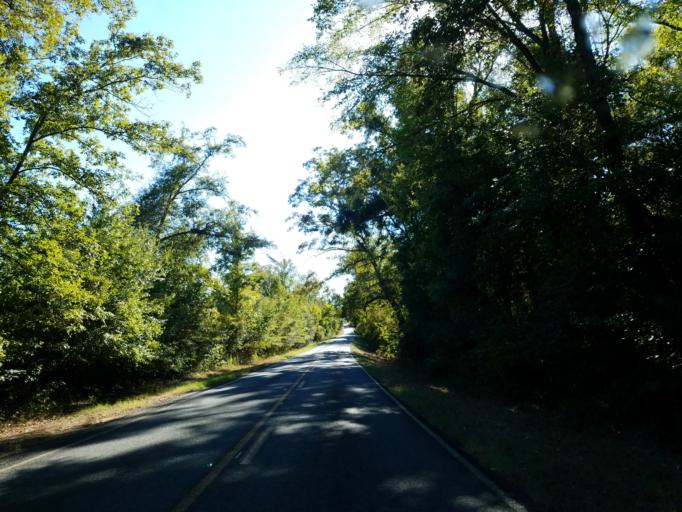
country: US
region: Georgia
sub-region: Dooly County
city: Unadilla
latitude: 32.2346
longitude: -83.8737
